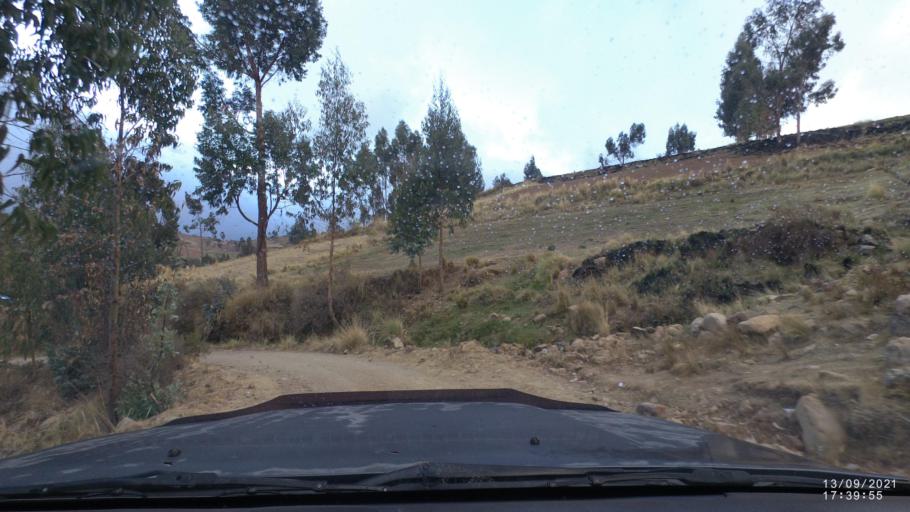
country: BO
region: Cochabamba
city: Colomi
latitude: -17.3627
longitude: -65.8092
